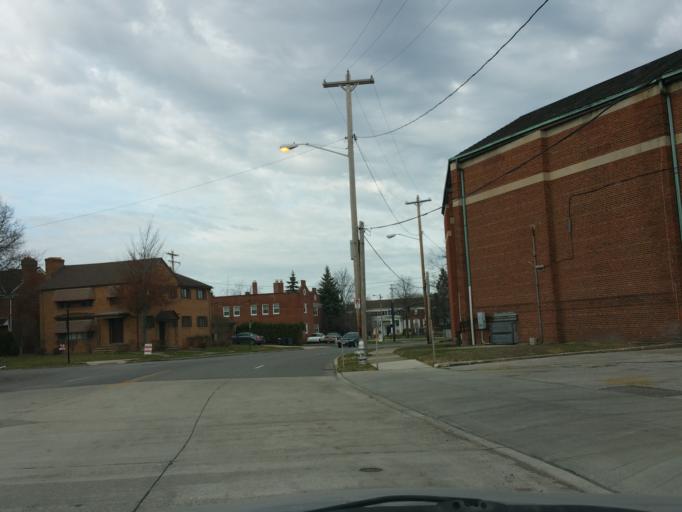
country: US
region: Ohio
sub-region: Cuyahoga County
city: Shaker Heights
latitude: 41.4652
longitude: -81.5391
